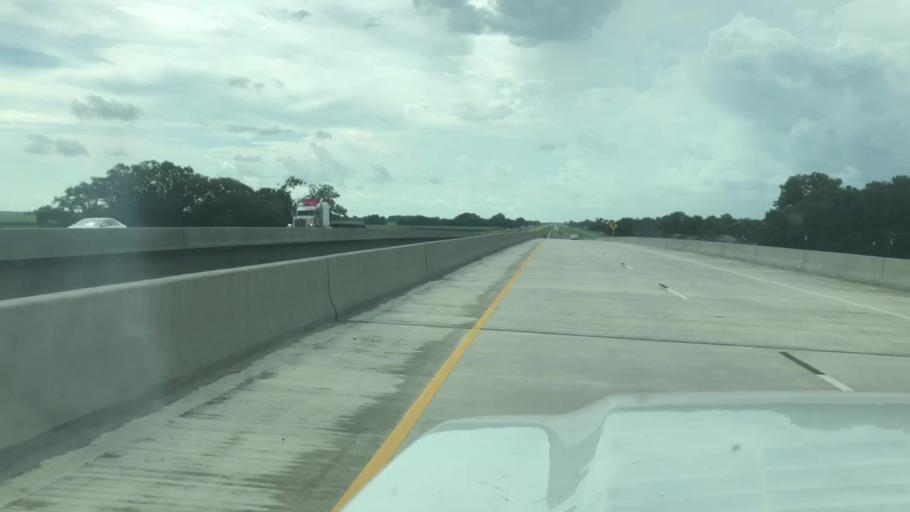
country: US
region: Louisiana
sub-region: Iberia Parish
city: Jeanerette
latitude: 29.8667
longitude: -91.6336
